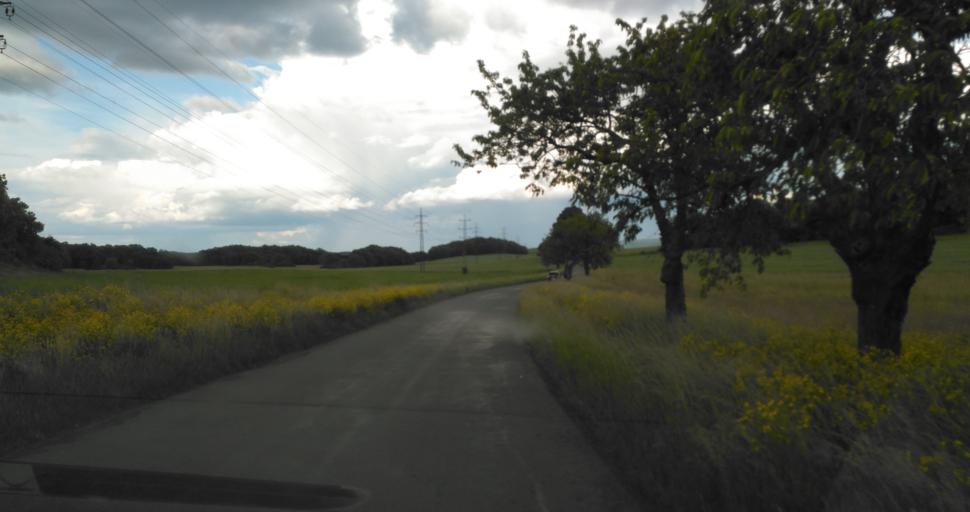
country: CZ
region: Central Bohemia
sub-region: Okres Beroun
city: Beroun
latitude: 49.9242
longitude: 14.1121
